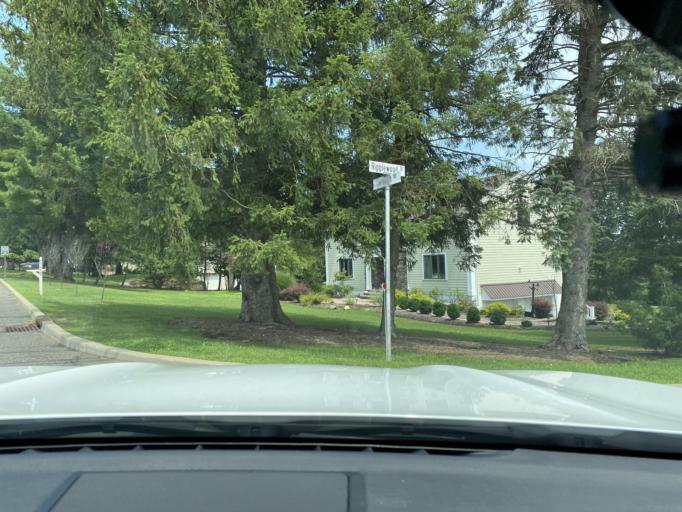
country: US
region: New Jersey
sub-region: Bergen County
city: Upper Saddle River
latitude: 41.0753
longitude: -74.1118
